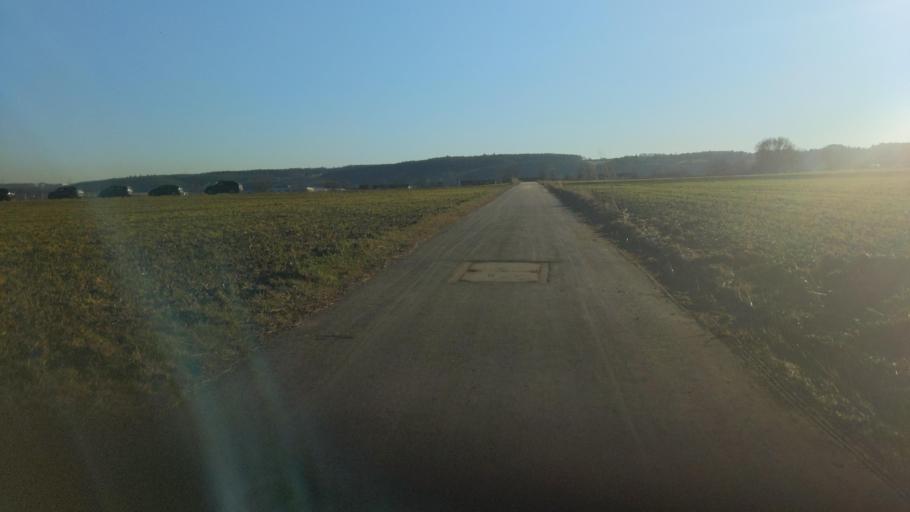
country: DE
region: Baden-Wuerttemberg
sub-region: Regierungsbezirk Stuttgart
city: Renningen
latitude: 48.7819
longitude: 8.9101
